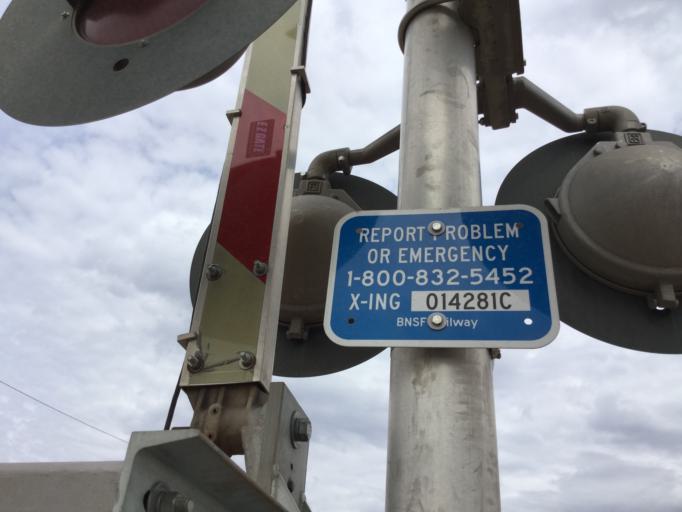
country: US
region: Kansas
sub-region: Barber County
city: Kiowa
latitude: 37.0962
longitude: -98.4026
